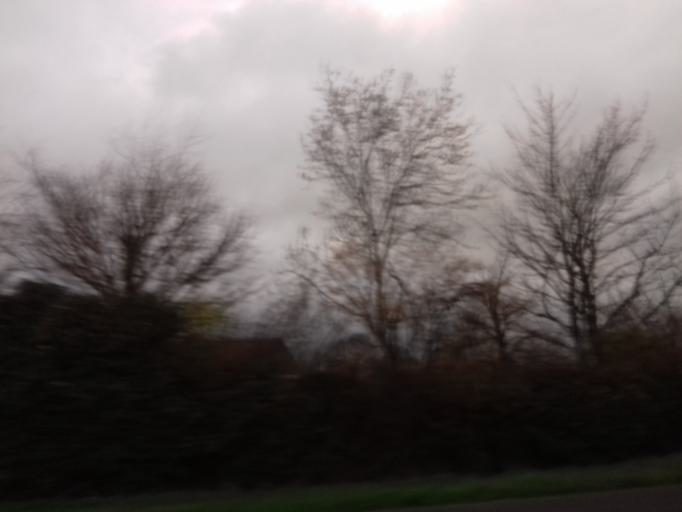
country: IE
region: Munster
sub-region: County Limerick
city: Newcastle West
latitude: 52.4684
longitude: -9.0236
